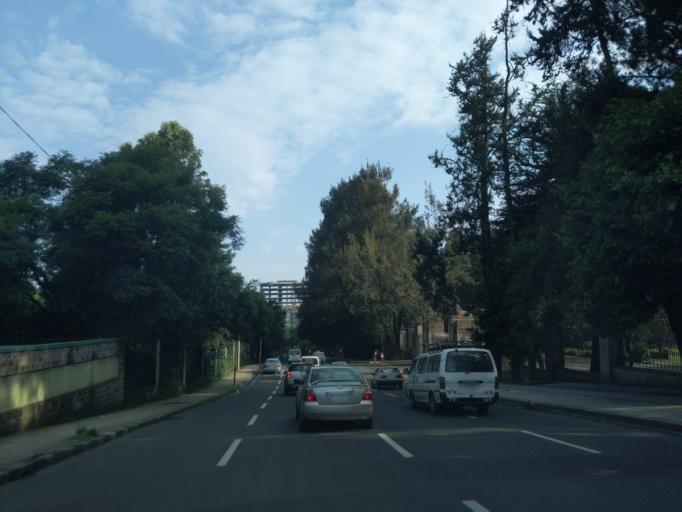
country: ET
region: Adis Abeba
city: Addis Ababa
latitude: 9.0166
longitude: 38.7629
